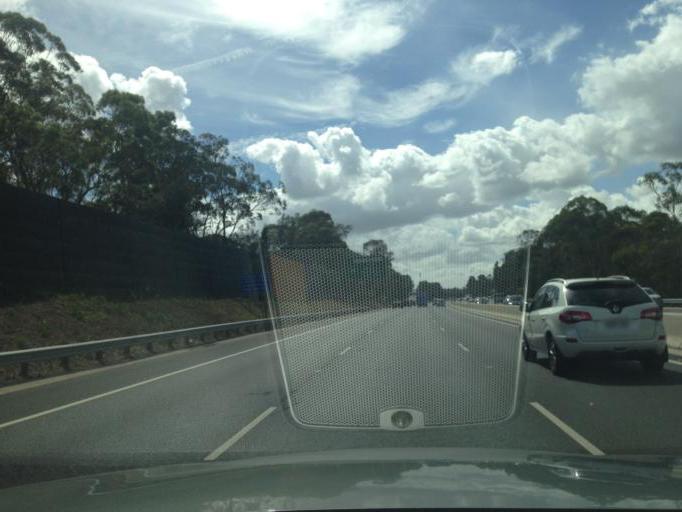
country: AU
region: New South Wales
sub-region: Bankstown
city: Milperra
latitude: -33.9457
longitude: 150.9748
